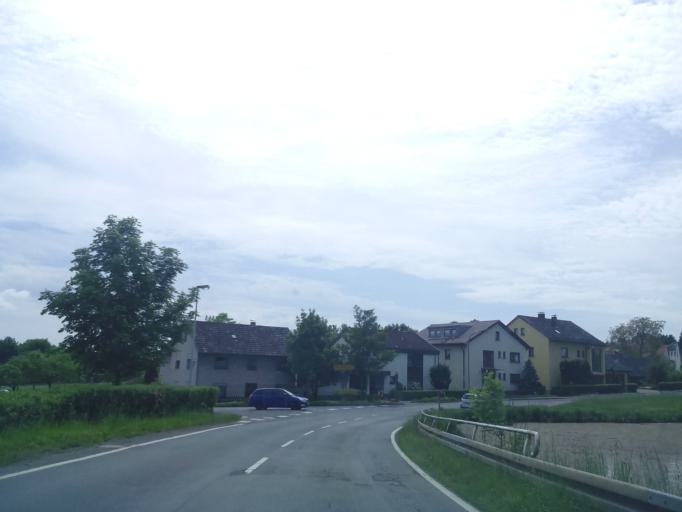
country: DE
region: Bavaria
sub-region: Upper Franconia
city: Ahorn
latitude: 50.2590
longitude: 10.9223
